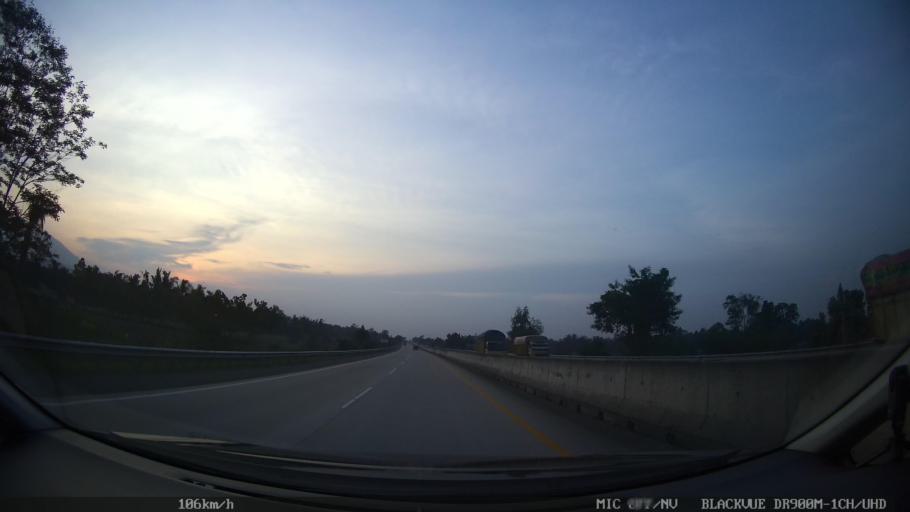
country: ID
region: Lampung
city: Penengahan
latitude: -5.7471
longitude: 105.7033
